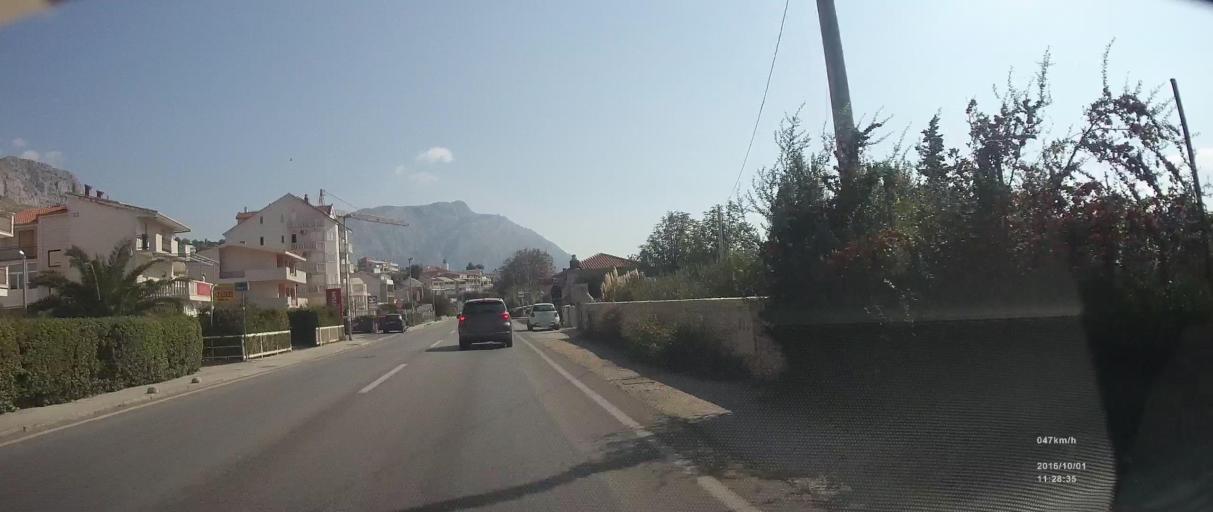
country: HR
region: Splitsko-Dalmatinska
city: Duce
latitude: 43.4409
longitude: 16.6593
